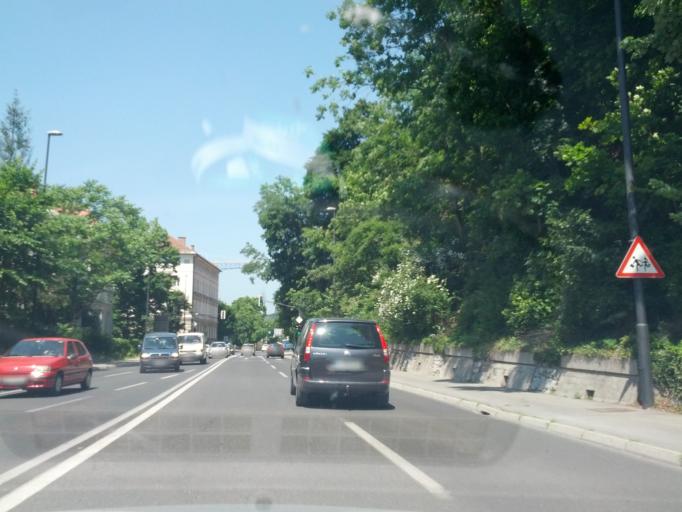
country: SI
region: Ljubljana
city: Ljubljana
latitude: 46.0430
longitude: 14.5132
